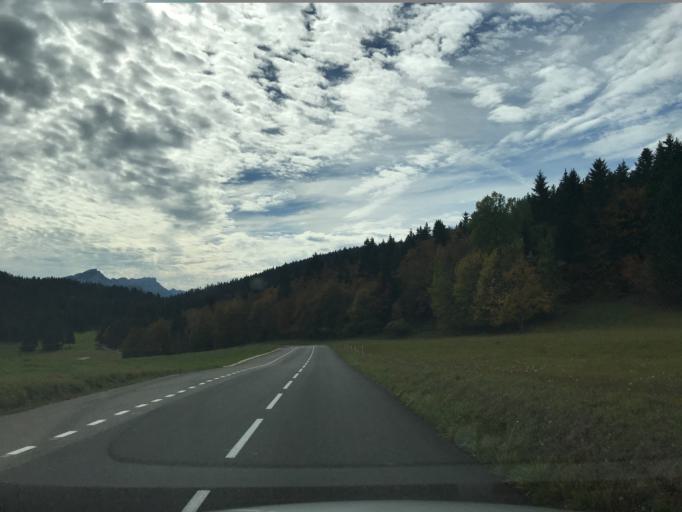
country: FR
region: Rhone-Alpes
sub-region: Departement de la Savoie
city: Vimines
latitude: 45.4588
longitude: 5.8579
